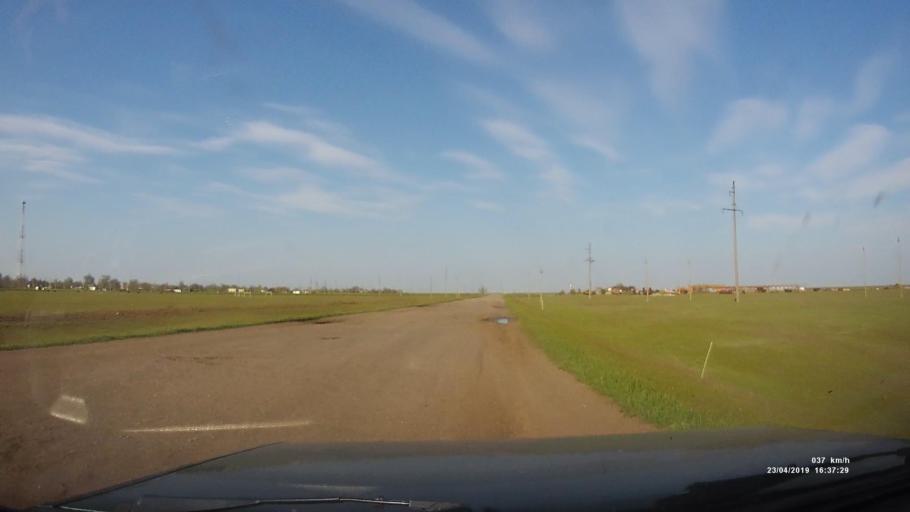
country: RU
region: Kalmykiya
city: Priyutnoye
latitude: 46.3325
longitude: 43.1465
